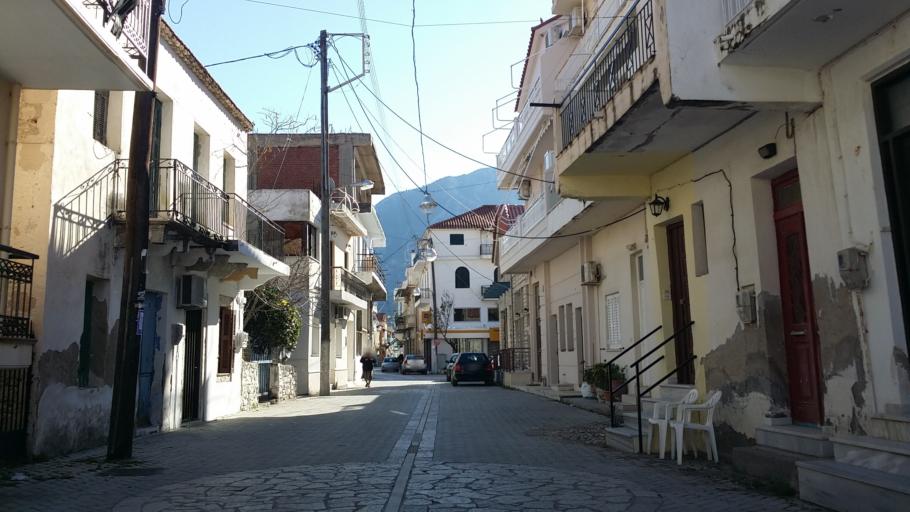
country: GR
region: West Greece
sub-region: Nomos Aitolias kai Akarnanias
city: Kandila
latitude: 38.6694
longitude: 20.9434
